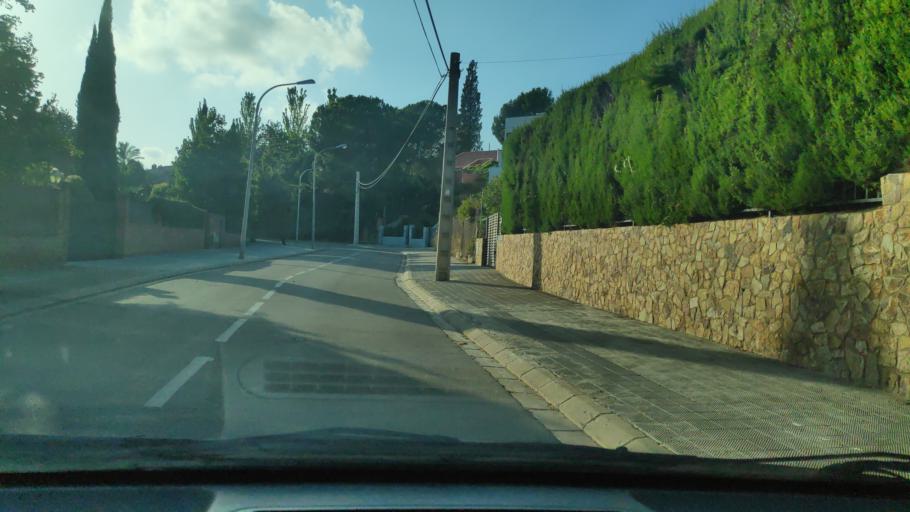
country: ES
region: Catalonia
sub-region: Provincia de Barcelona
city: Sant Cugat del Valles
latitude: 41.4983
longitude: 2.0834
